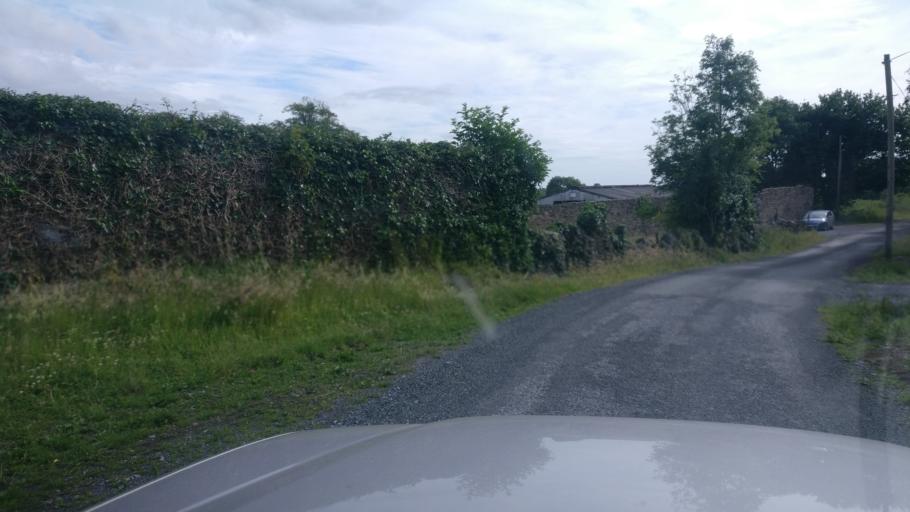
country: IE
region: Connaught
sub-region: County Galway
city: Gort
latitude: 53.1095
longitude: -8.7243
